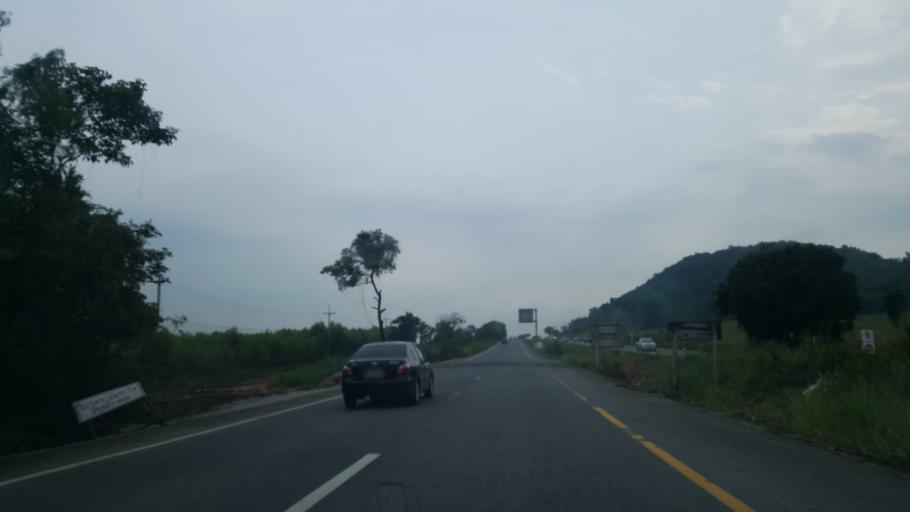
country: TH
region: Rayong
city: Ban Chang
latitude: 12.7626
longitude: 100.9917
